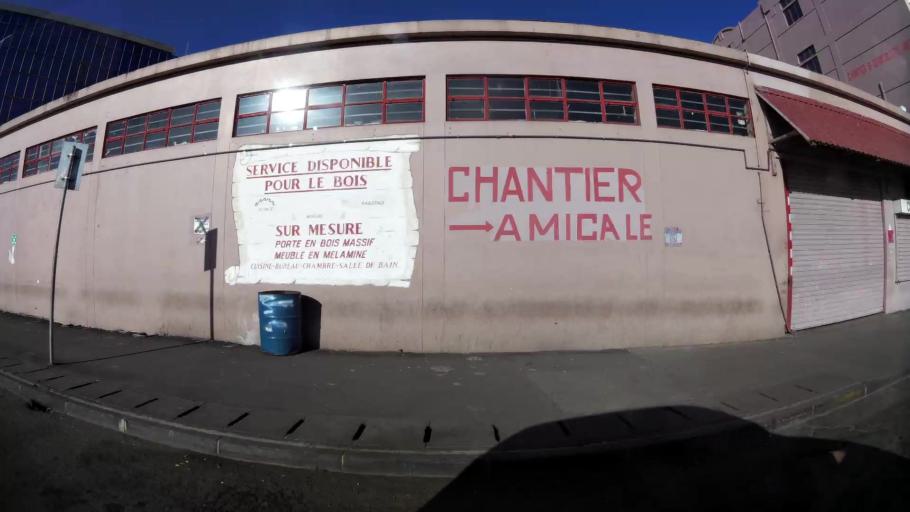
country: MU
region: Port Louis
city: Port Louis
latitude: -20.1573
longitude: 57.5059
